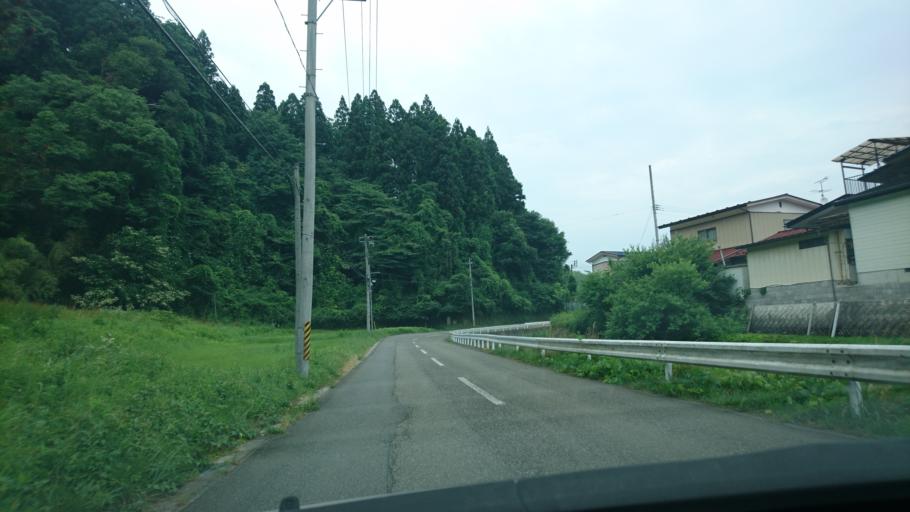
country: JP
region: Iwate
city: Ichinoseki
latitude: 38.9105
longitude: 141.1212
